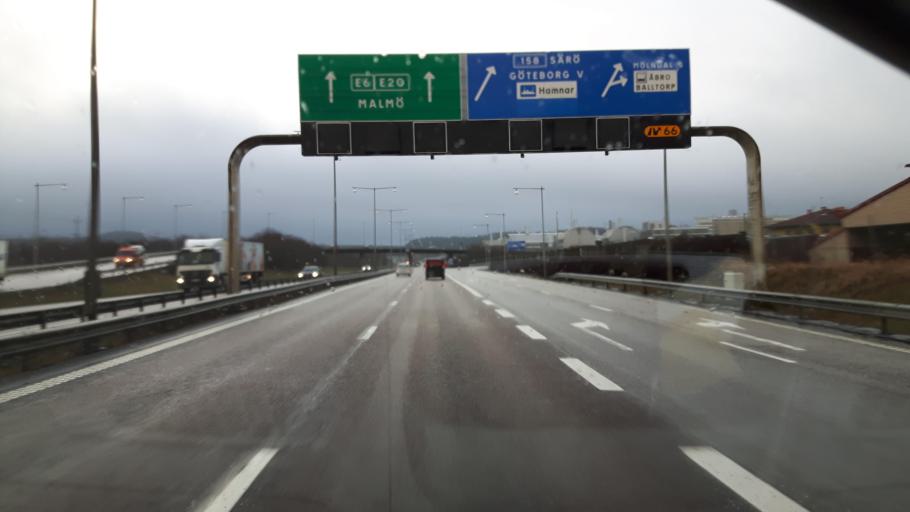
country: SE
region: Vaestra Goetaland
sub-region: Molndal
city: Moelndal
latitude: 57.6503
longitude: 12.0207
